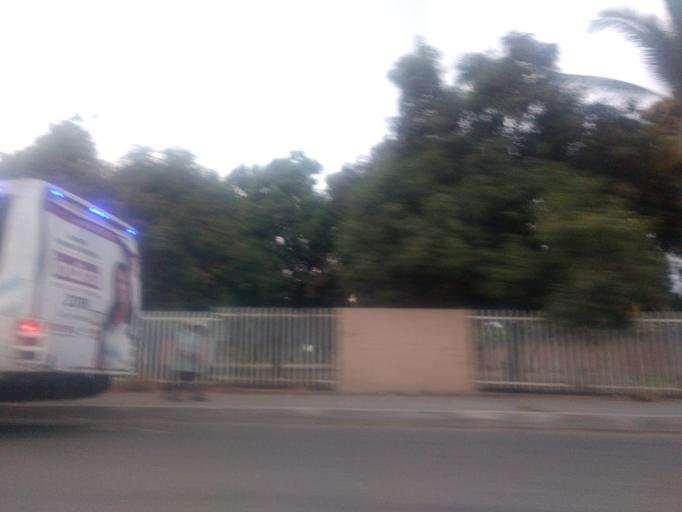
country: MX
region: Colima
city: Tapeixtles
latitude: 19.0884
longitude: -104.2934
